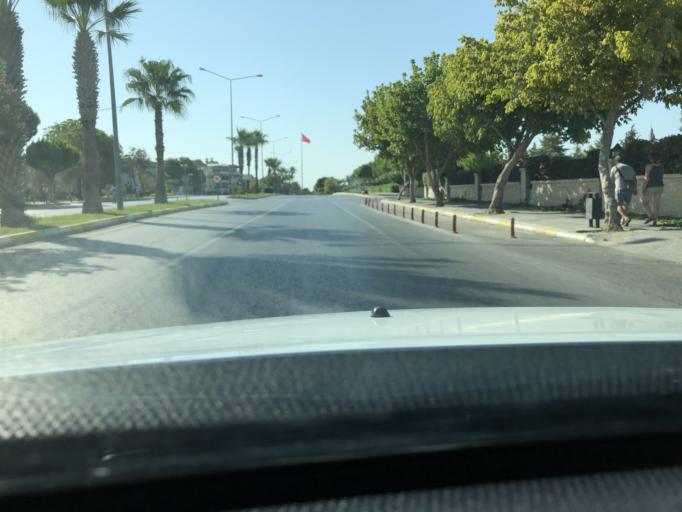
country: TR
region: Antalya
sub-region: Manavgat
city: Side
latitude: 36.7803
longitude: 31.3941
